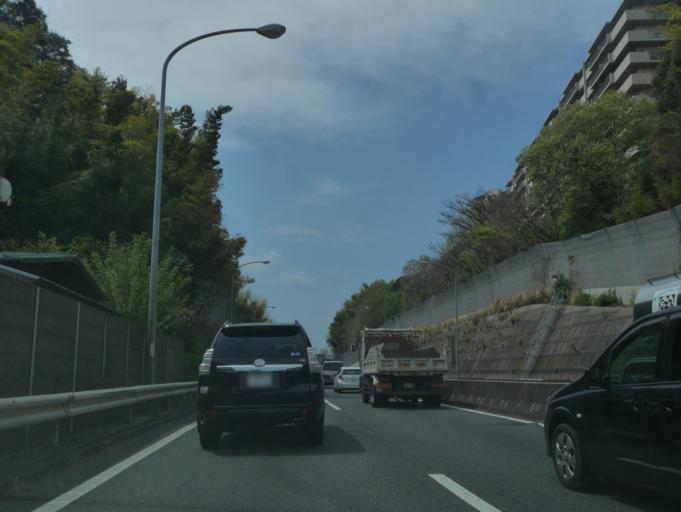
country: JP
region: Kanagawa
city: Fujisawa
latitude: 35.4155
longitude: 139.5361
